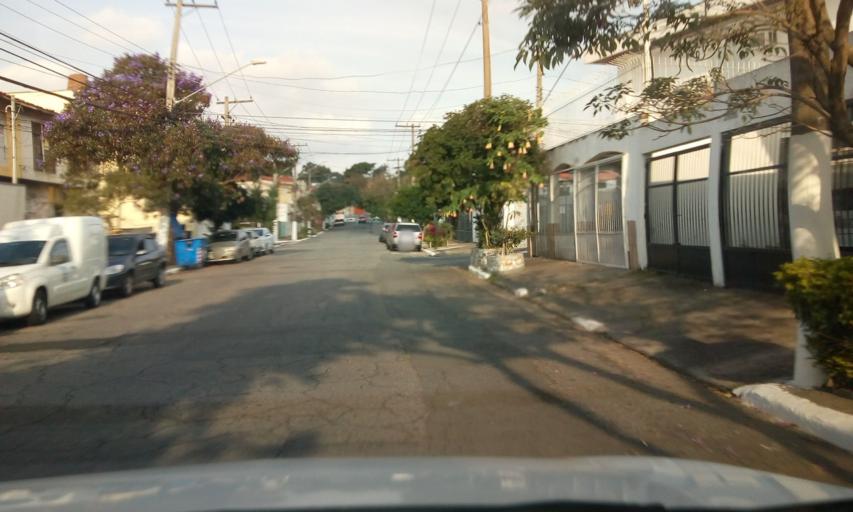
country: BR
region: Sao Paulo
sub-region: Diadema
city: Diadema
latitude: -23.6203
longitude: -46.6511
